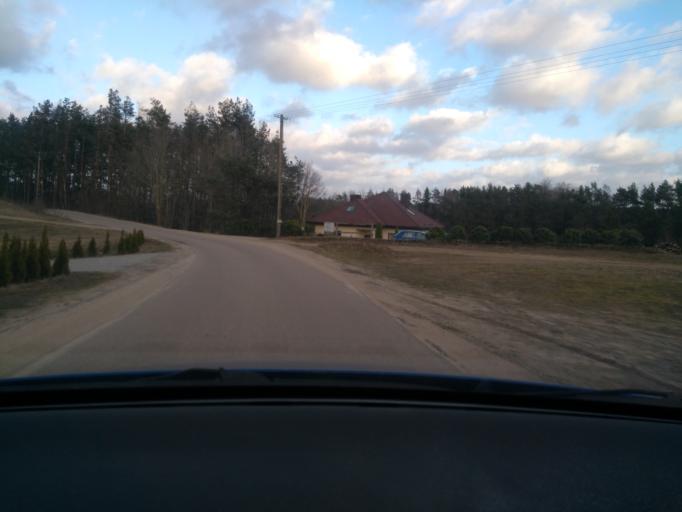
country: PL
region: Pomeranian Voivodeship
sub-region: Powiat kartuski
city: Przodkowo
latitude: 54.4127
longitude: 18.2362
